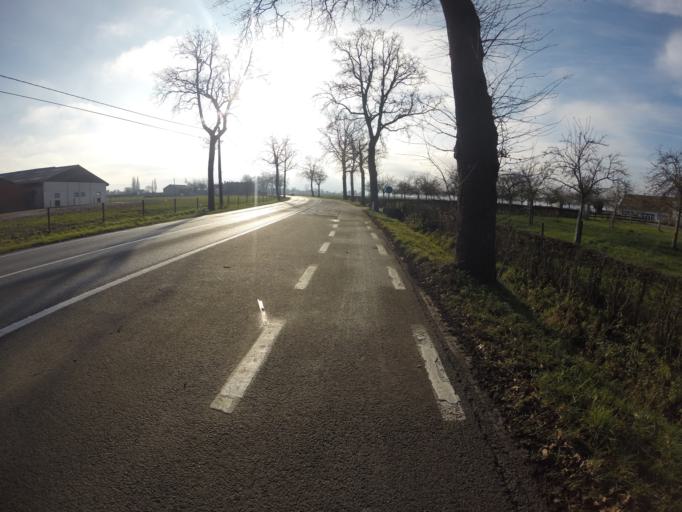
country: BE
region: Flanders
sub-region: Provincie Oost-Vlaanderen
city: Aalter
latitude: 51.0370
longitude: 3.4646
